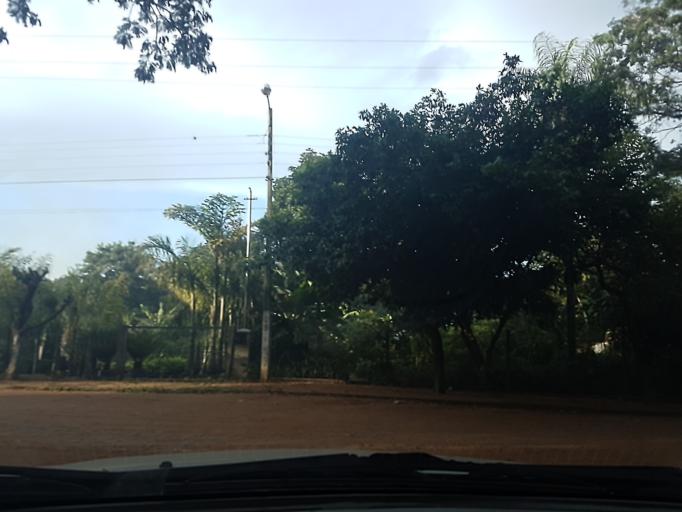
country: PY
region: Central
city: Limpio
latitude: -25.2405
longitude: -57.4608
